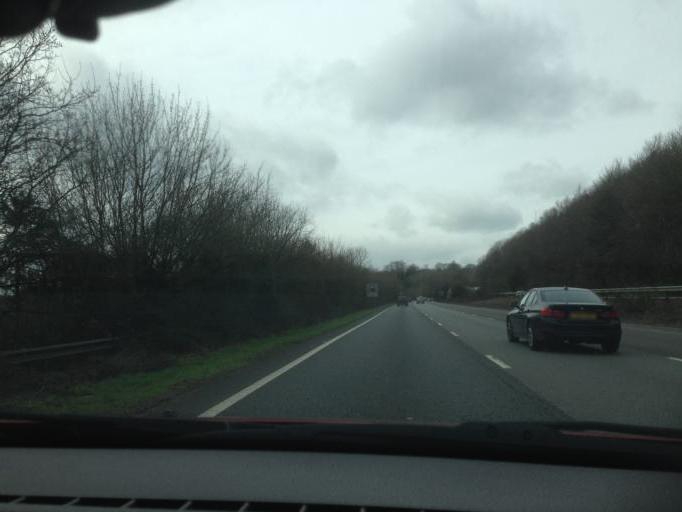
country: GB
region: England
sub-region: Kent
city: Sevenoaks
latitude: 51.2461
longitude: 0.1851
